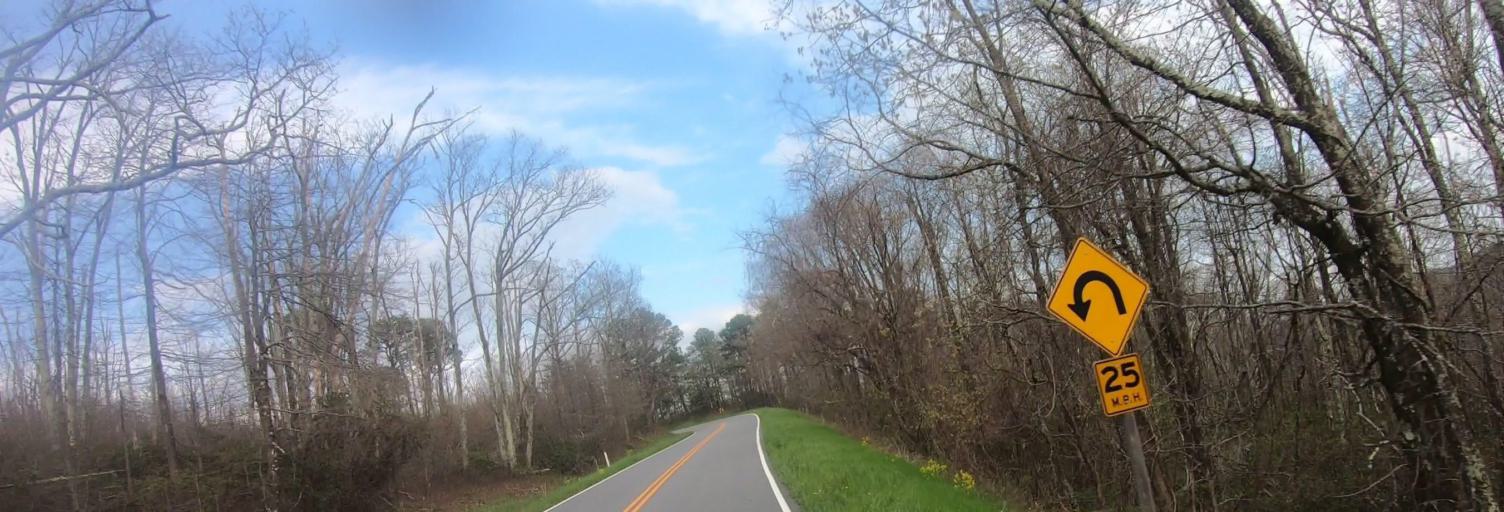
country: US
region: Virginia
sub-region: Rockingham County
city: Grottoes
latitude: 38.2099
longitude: -78.7341
